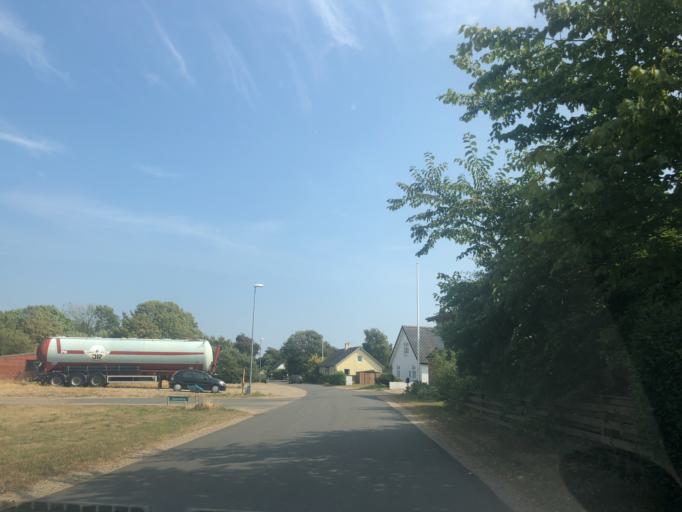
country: DK
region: North Denmark
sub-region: Morso Kommune
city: Nykobing Mors
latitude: 56.8198
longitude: 9.0049
